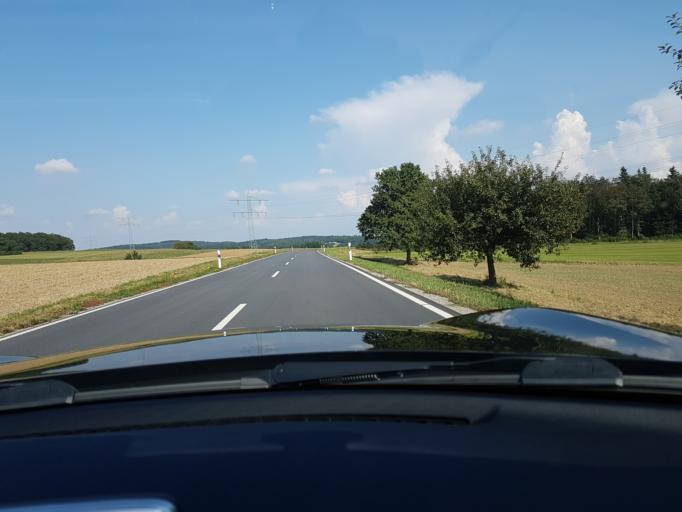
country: DE
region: Baden-Wuerttemberg
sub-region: Karlsruhe Region
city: Osterburken
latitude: 49.4761
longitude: 9.3849
